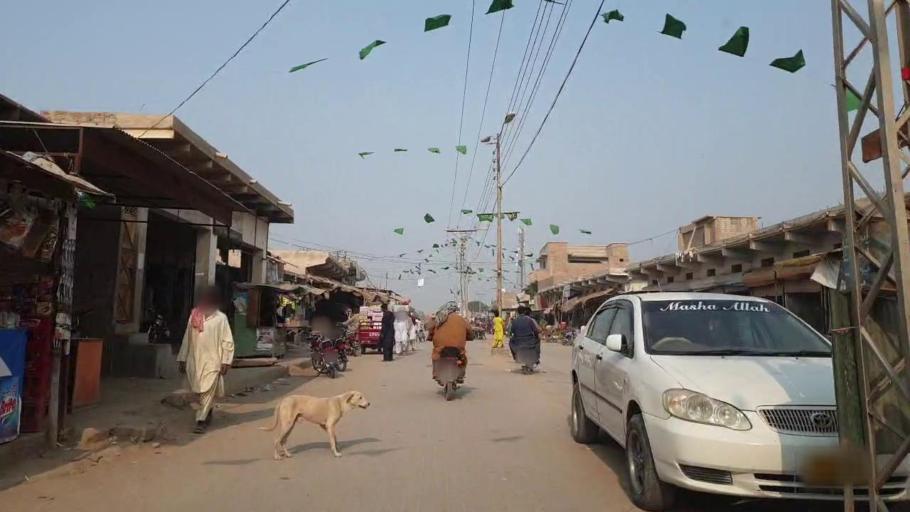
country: PK
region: Sindh
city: Bhan
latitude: 26.5618
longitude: 67.7224
